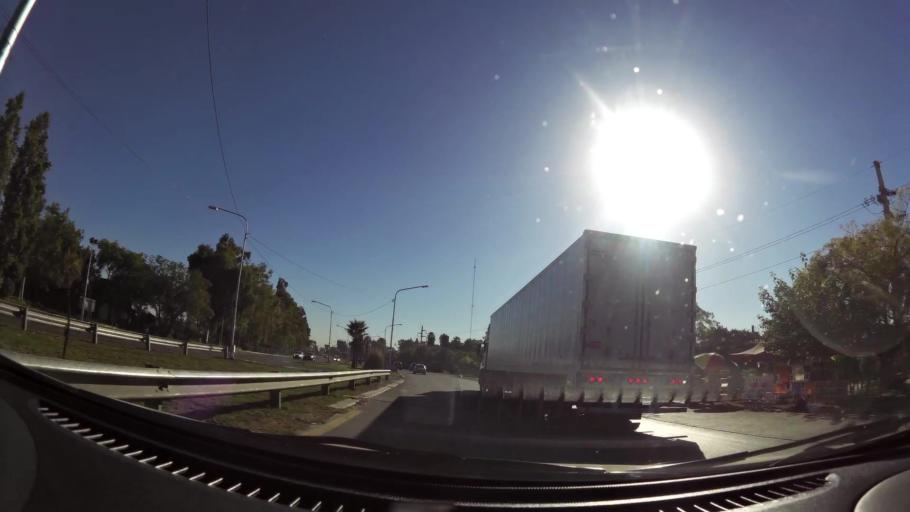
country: AR
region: Mendoza
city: Las Heras
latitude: -32.8706
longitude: -68.8154
